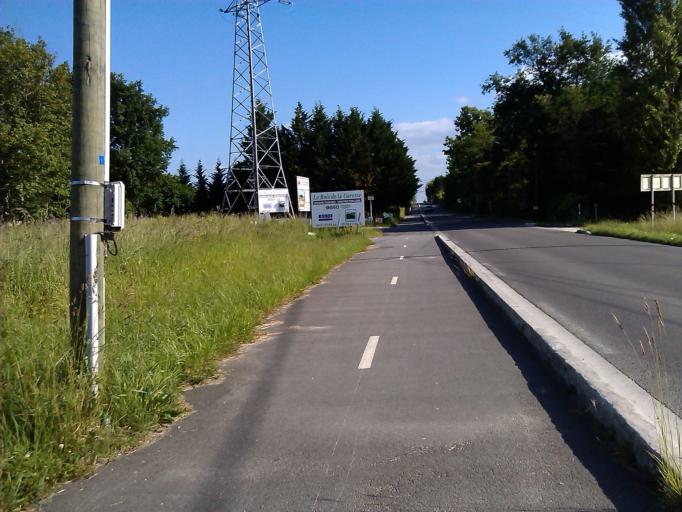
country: FR
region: Aquitaine
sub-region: Departement de la Gironde
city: Saint-Gervais
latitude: 45.0073
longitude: -0.4480
